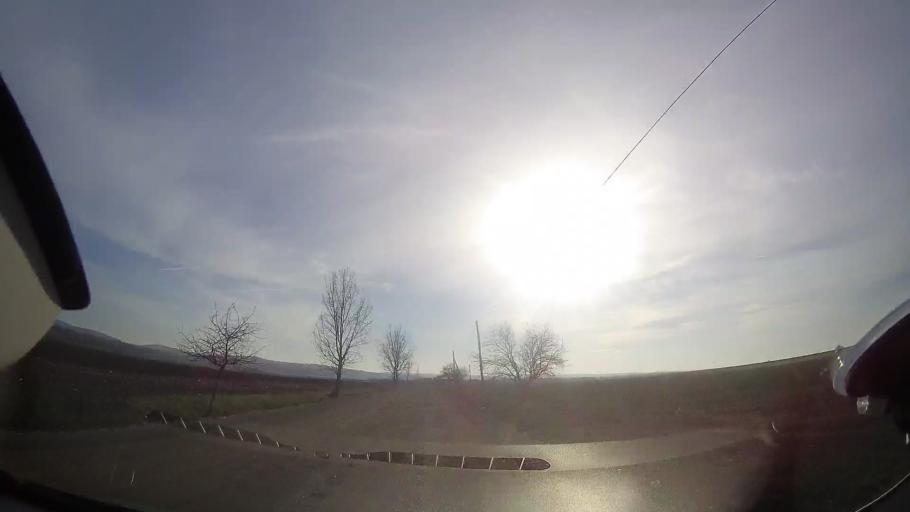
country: RO
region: Bihor
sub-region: Comuna Ciuhoiu
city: Ciuhoiu
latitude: 47.2222
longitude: 22.1346
